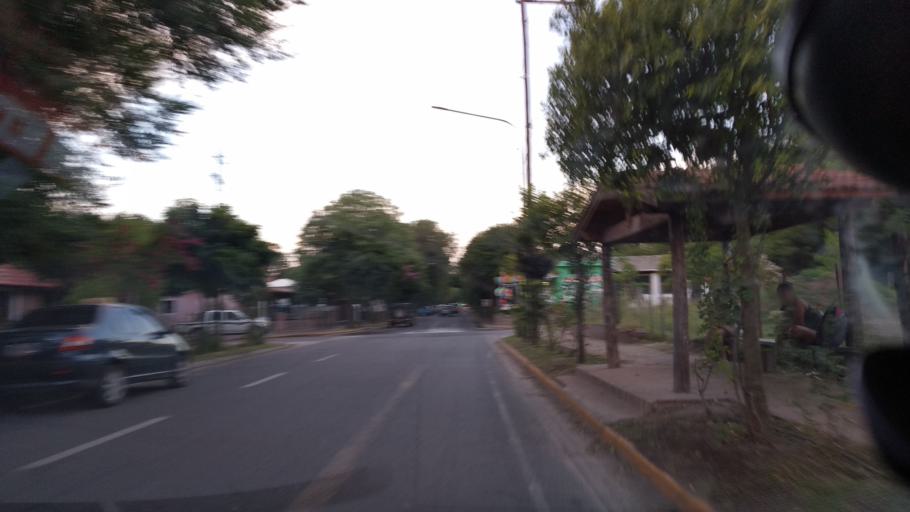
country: AR
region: Cordoba
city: Villa Las Rosas
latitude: -31.9509
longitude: -65.0529
